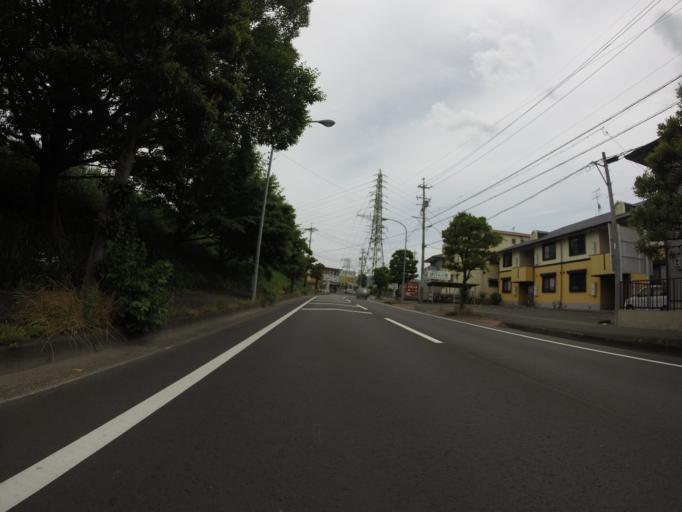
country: JP
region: Shizuoka
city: Shizuoka-shi
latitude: 35.0007
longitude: 138.4231
